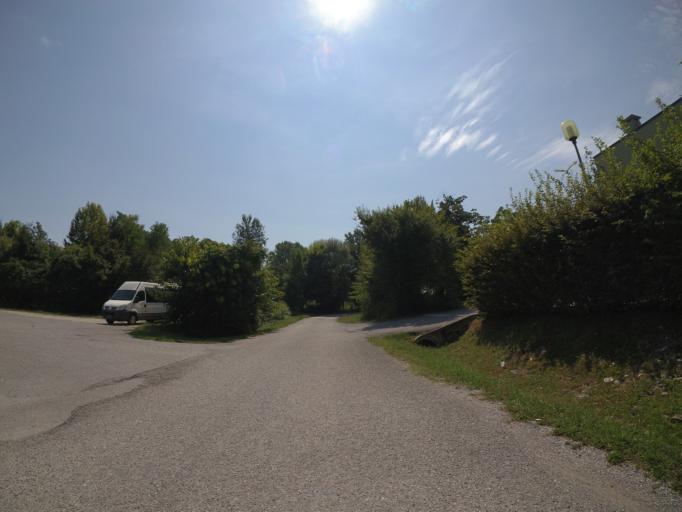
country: IT
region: Friuli Venezia Giulia
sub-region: Provincia di Udine
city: Codroipo
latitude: 45.9557
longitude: 12.9784
